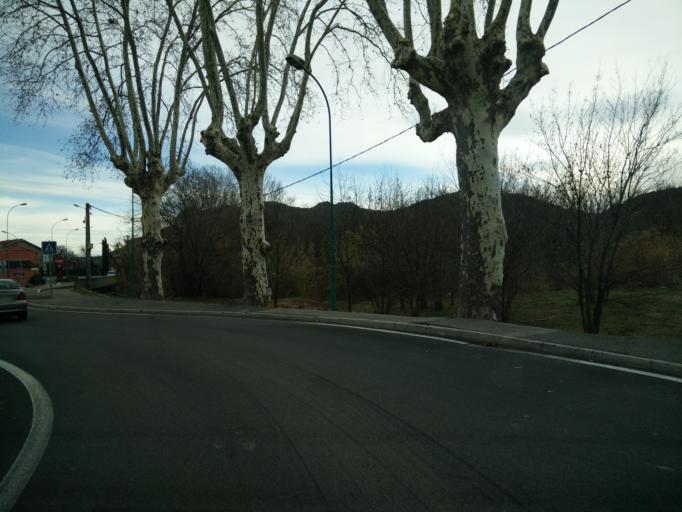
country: FR
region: Provence-Alpes-Cote d'Azur
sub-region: Departement du Var
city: Le Muy
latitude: 43.4715
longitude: 6.5724
